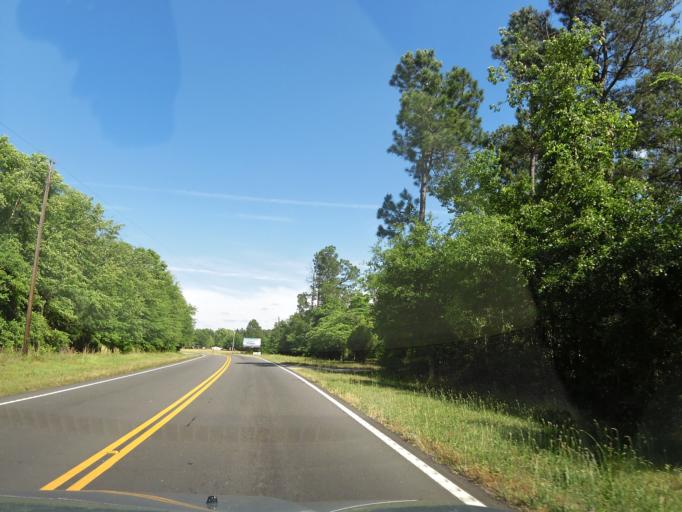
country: US
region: South Carolina
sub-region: Barnwell County
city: Williston
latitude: 33.4143
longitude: -81.4693
